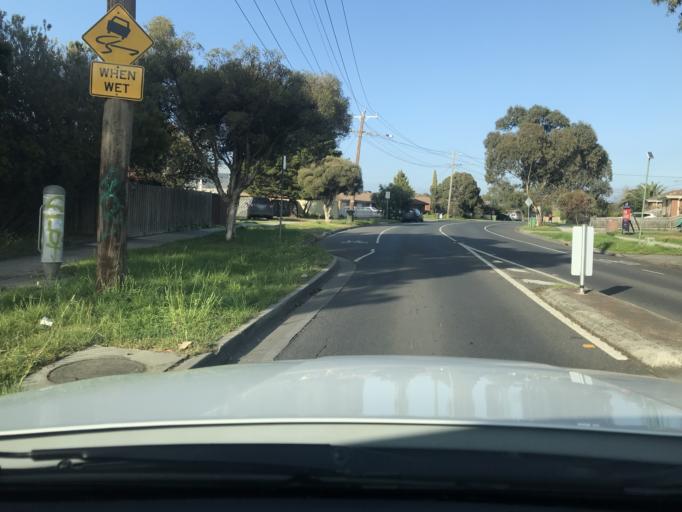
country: AU
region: Victoria
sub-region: Hume
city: Craigieburn
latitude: -37.6036
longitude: 144.9418
